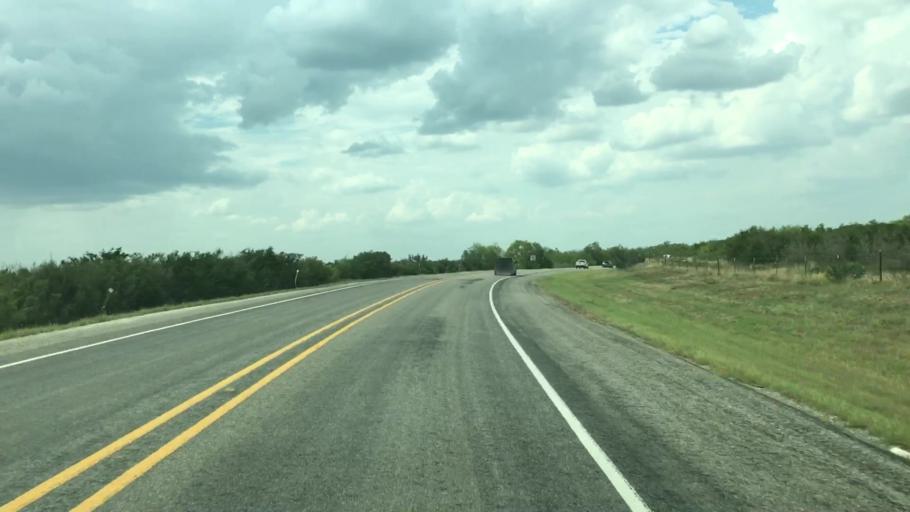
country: US
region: Texas
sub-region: Live Oak County
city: Three Rivers
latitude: 28.6416
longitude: -98.2831
